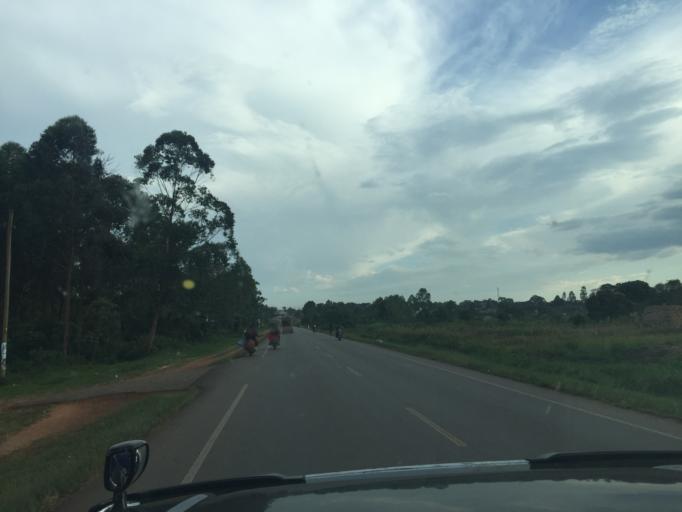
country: UG
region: Central Region
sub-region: Luwero District
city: Luwero
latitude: 0.8582
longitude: 32.4863
